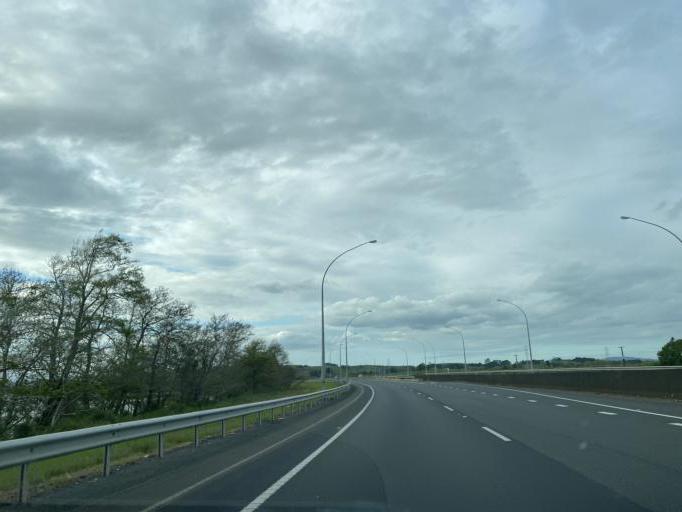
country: NZ
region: Waikato
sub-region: Waikato District
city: Te Kauwhata
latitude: -37.3112
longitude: 175.0672
